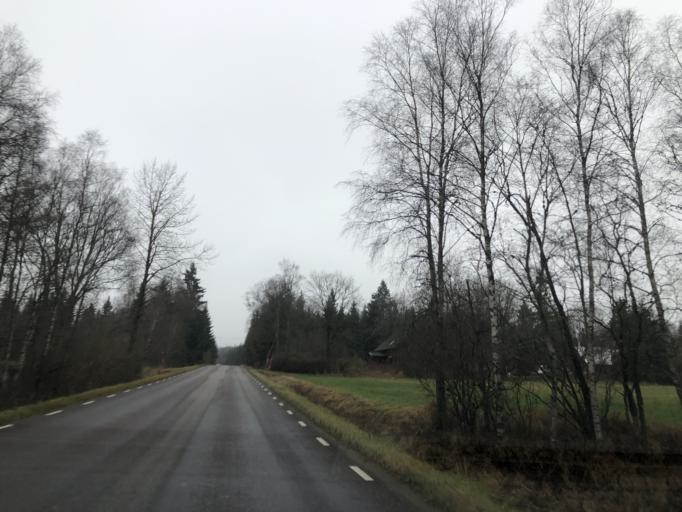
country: SE
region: Vaestra Goetaland
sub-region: Ulricehamns Kommun
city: Ulricehamn
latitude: 57.7457
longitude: 13.5322
